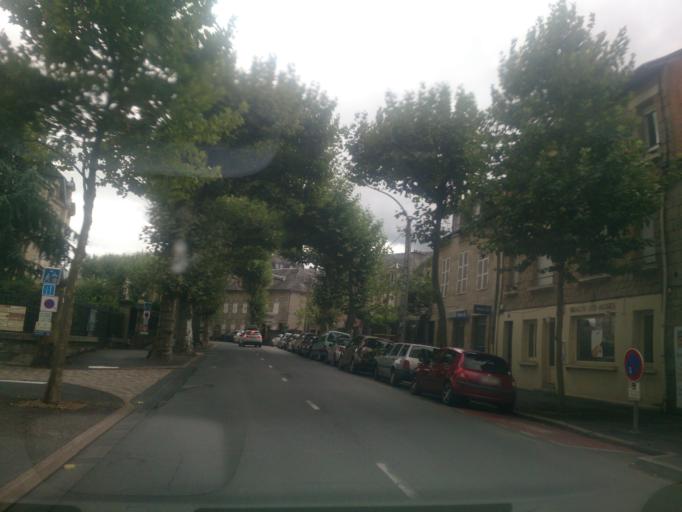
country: FR
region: Limousin
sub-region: Departement de la Correze
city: Brive-la-Gaillarde
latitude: 45.1573
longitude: 1.5301
